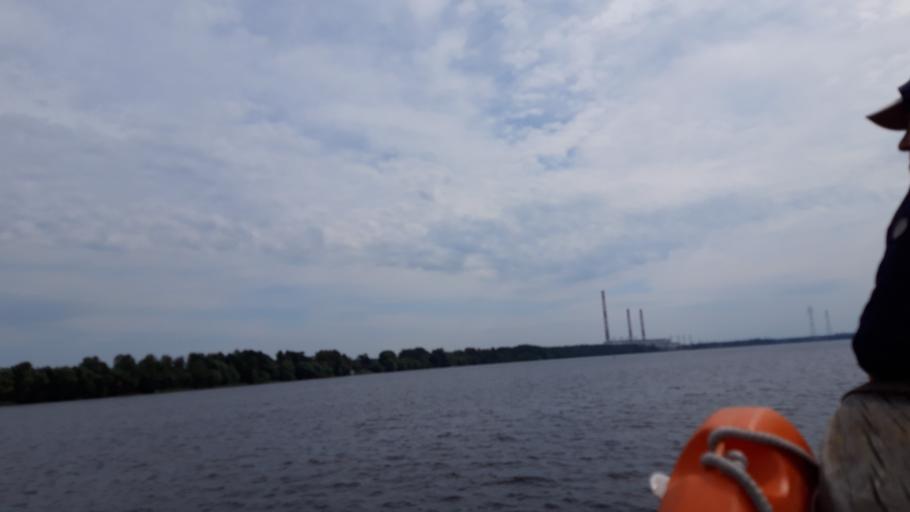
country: RU
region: Tverskaya
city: Konakovo
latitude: 56.7592
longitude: 36.7372
